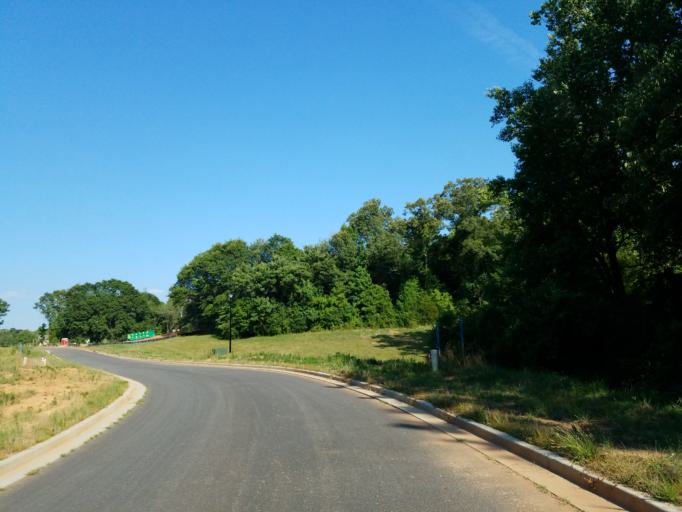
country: US
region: Georgia
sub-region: Fulton County
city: Milton
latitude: 34.1765
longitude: -84.3315
